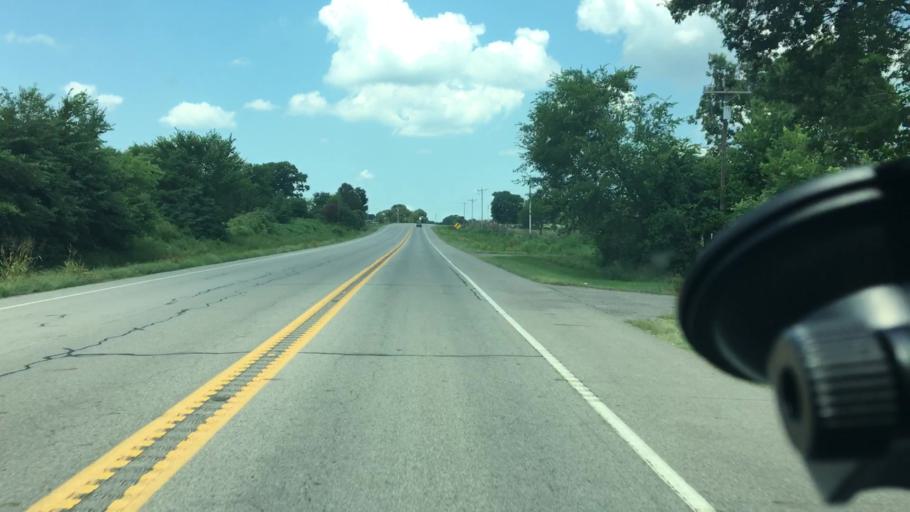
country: US
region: Arkansas
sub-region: Logan County
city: Paris
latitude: 35.2988
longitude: -93.8238
